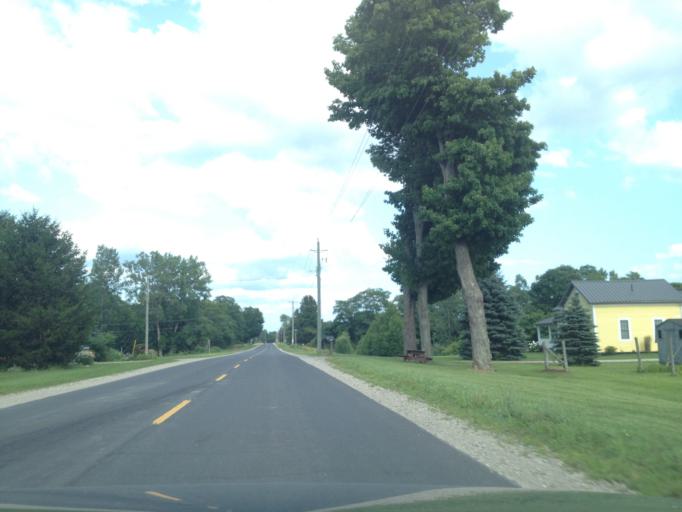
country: CA
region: Ontario
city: Aylmer
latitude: 42.6744
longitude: -80.9123
